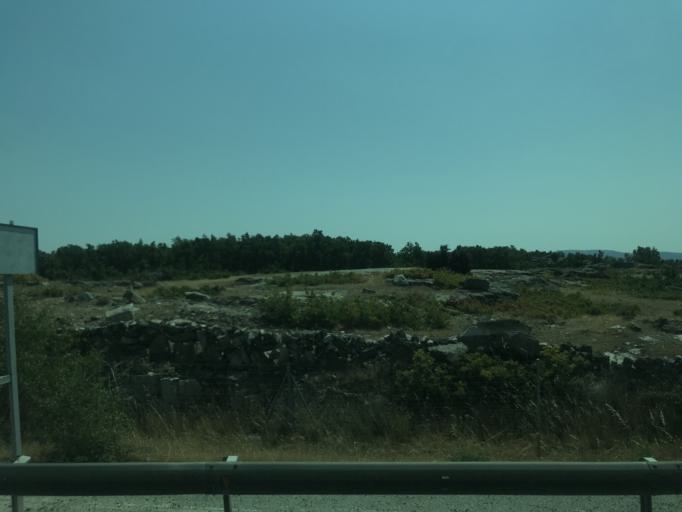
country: ES
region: Madrid
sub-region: Provincia de Madrid
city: La Cabrera
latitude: 40.9141
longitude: -3.6091
